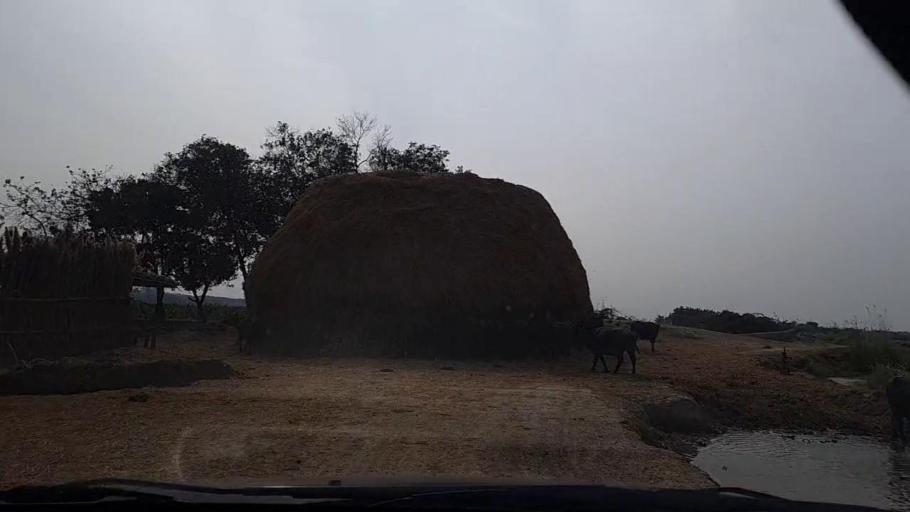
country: PK
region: Sindh
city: Thatta
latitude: 24.5736
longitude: 67.8794
